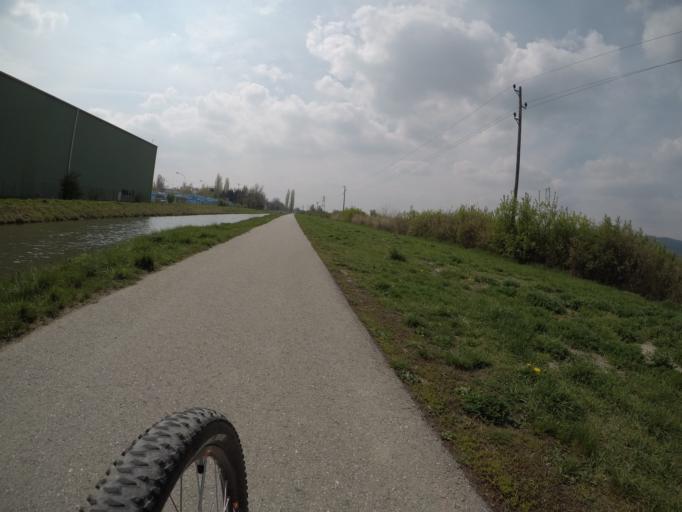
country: AT
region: Lower Austria
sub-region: Politischer Bezirk Modling
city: Gumpoldskirchen
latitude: 48.0321
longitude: 16.2873
